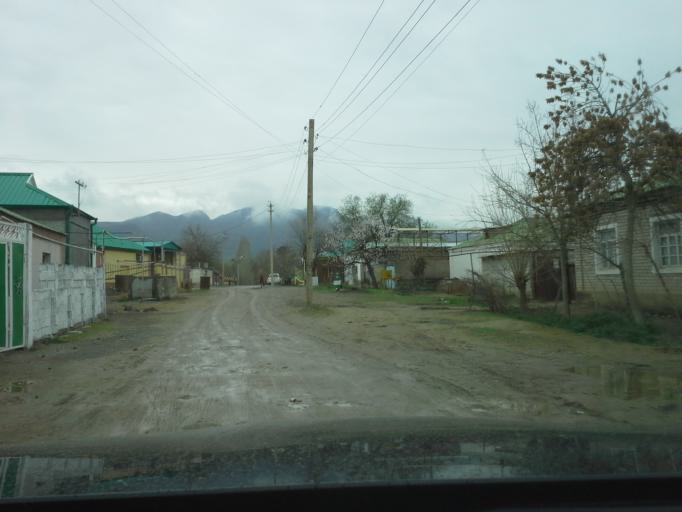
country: TM
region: Ahal
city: Abadan
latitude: 37.9623
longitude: 58.2260
